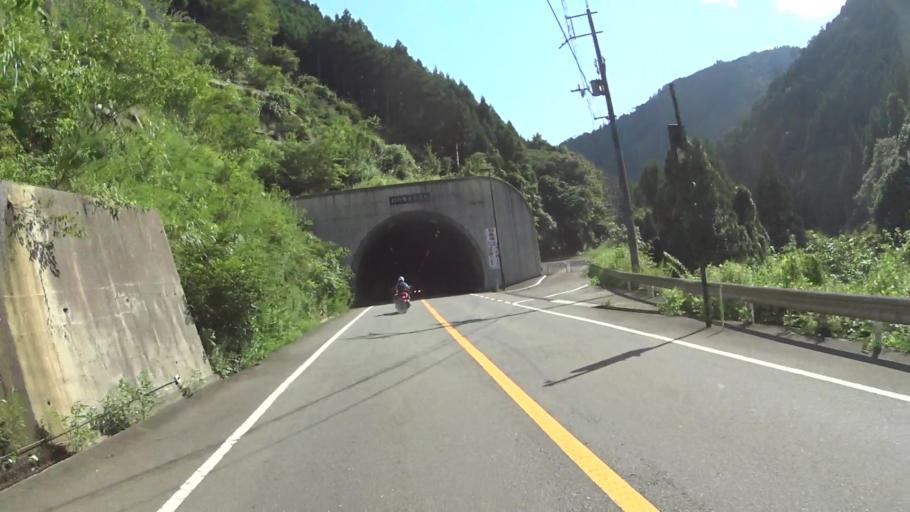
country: JP
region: Kyoto
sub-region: Kyoto-shi
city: Kamigyo-ku
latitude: 35.0794
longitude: 135.6869
